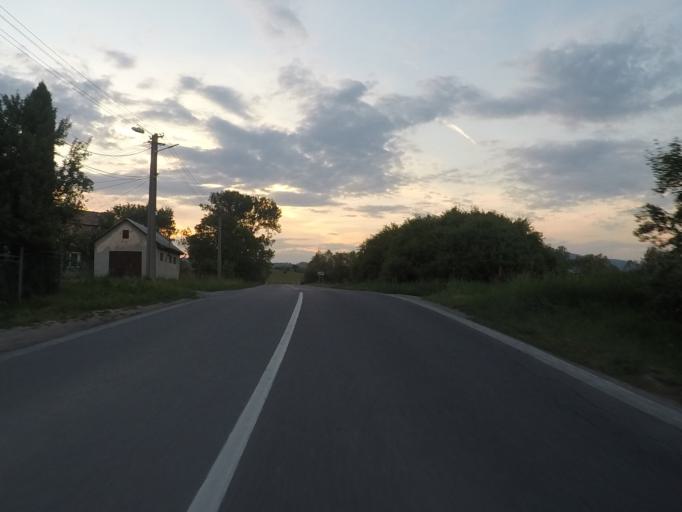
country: SK
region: Banskobystricky
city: Rimavska Sobota
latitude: 48.4531
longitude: 19.9565
